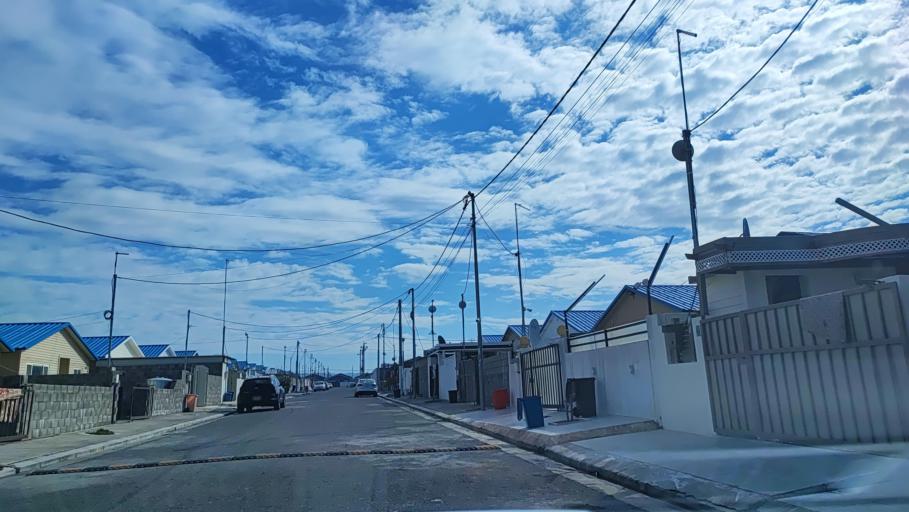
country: IQ
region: Arbil
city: Erbil
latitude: 36.2870
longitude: 44.0752
